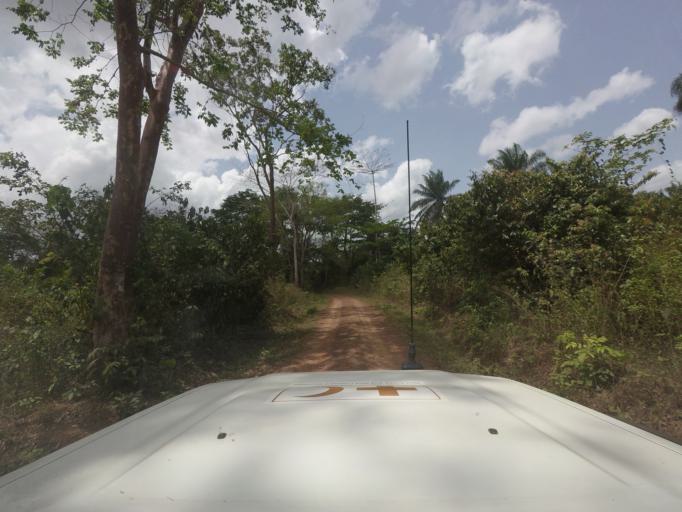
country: GN
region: Nzerekore
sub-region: Yomou
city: Yomou
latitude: 7.2787
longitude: -9.1861
